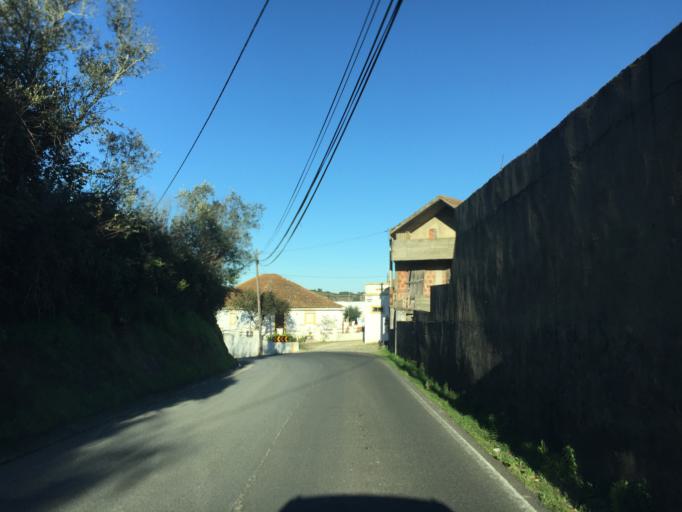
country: PT
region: Lisbon
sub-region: Odivelas
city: Canecas
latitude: 38.8237
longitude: -9.2360
